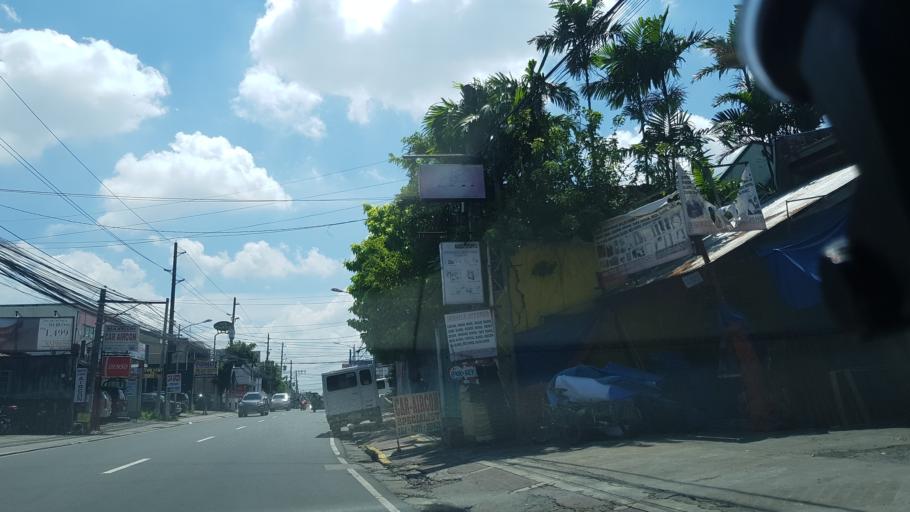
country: PH
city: Sambayanihan People's Village
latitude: 14.4553
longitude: 121.0310
